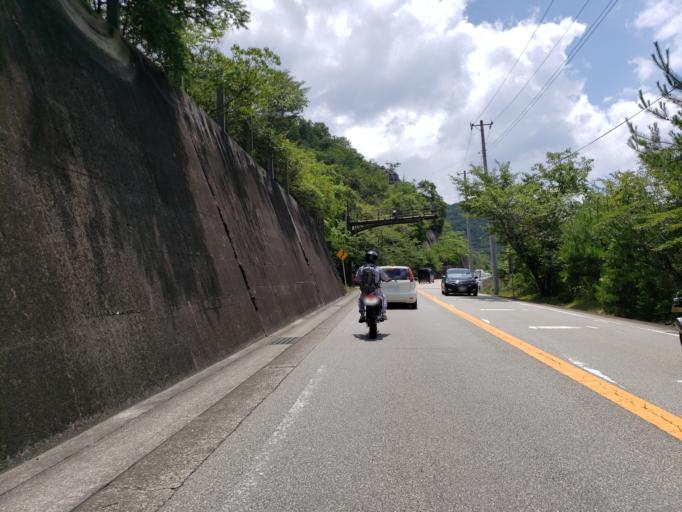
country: JP
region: Hyogo
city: Aioi
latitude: 34.7965
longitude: 134.4489
